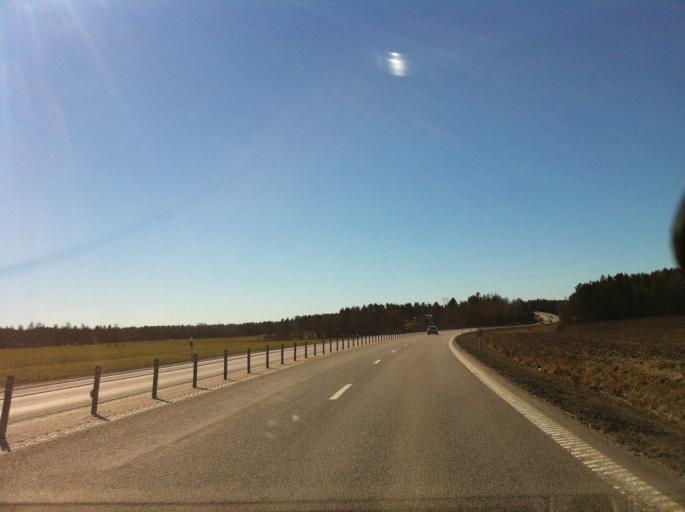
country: SE
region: Vaestra Goetaland
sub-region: Vanersborgs Kommun
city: Vargon
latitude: 58.3536
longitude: 12.3948
